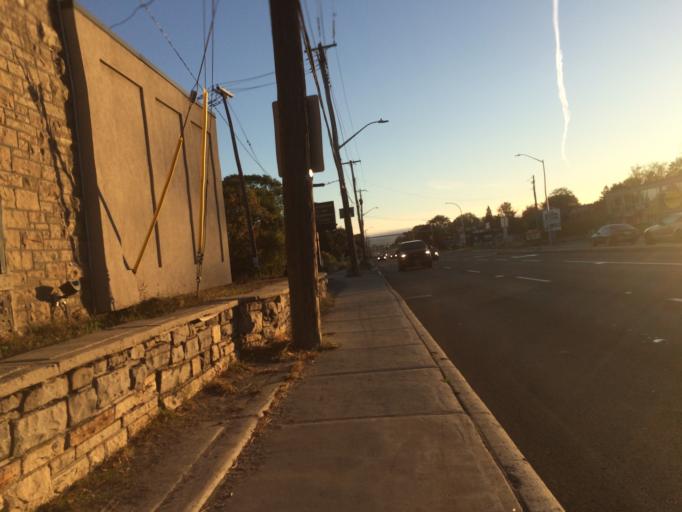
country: CA
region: Ontario
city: Bells Corners
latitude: 45.3249
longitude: -75.8266
